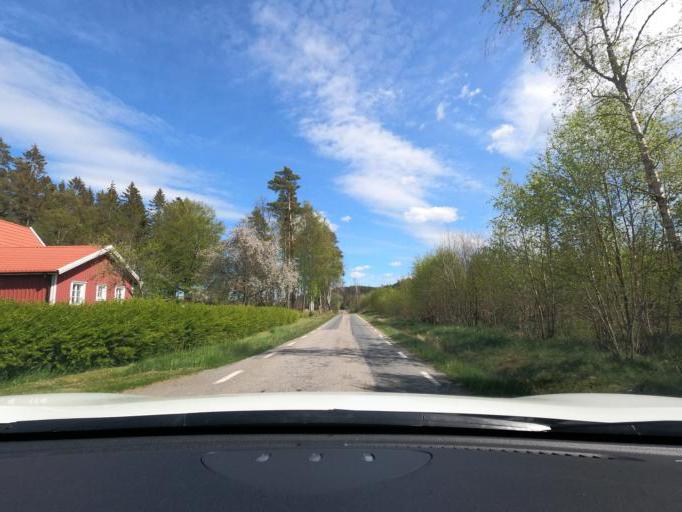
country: SE
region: Vaestra Goetaland
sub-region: Marks Kommun
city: Horred
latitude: 57.4509
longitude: 12.4541
